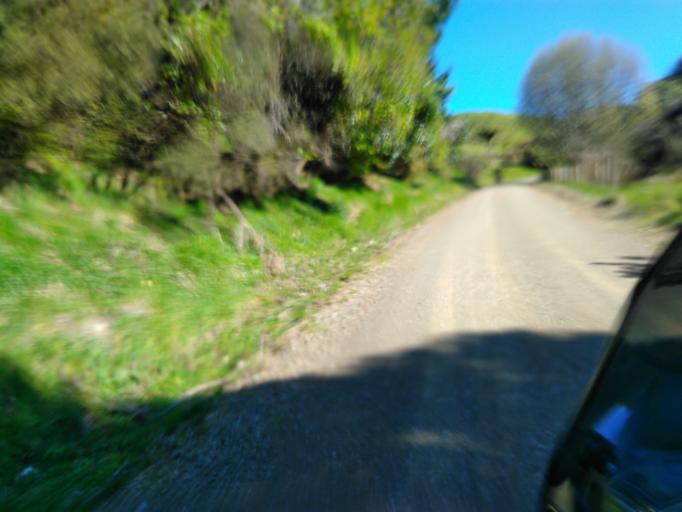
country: NZ
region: Bay of Plenty
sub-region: Opotiki District
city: Opotiki
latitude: -38.3676
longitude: 177.5973
